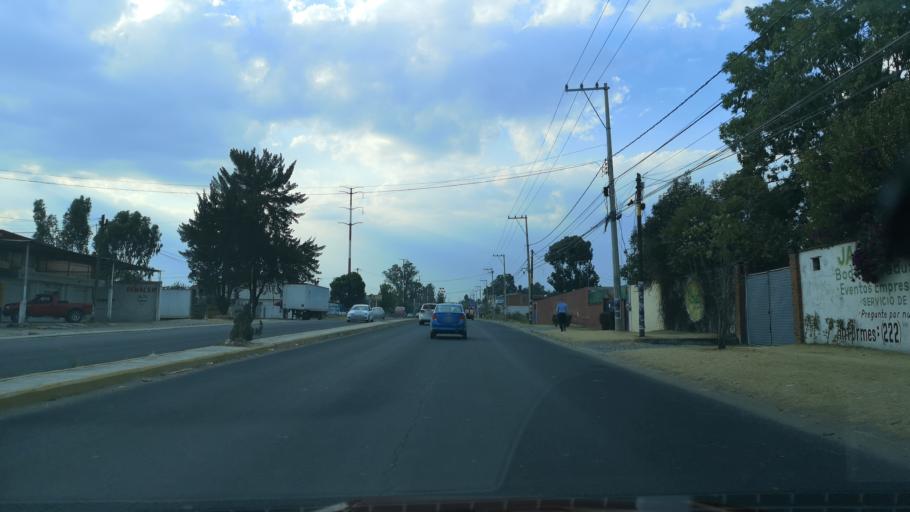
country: MX
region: Puebla
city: Cuanala
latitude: 19.0994
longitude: -98.3442
